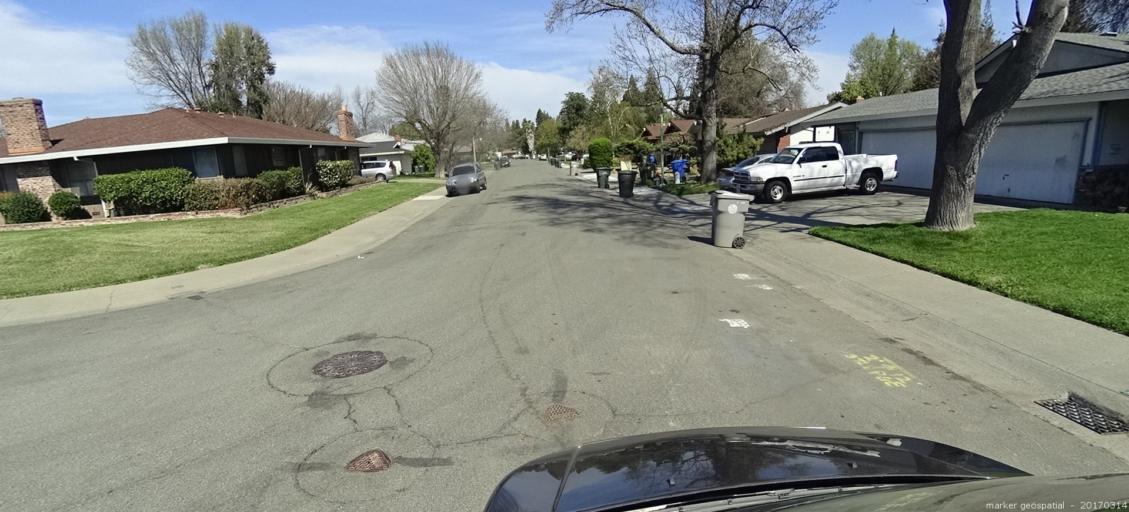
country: US
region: California
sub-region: Sacramento County
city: Parkway
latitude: 38.5113
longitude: -121.5231
